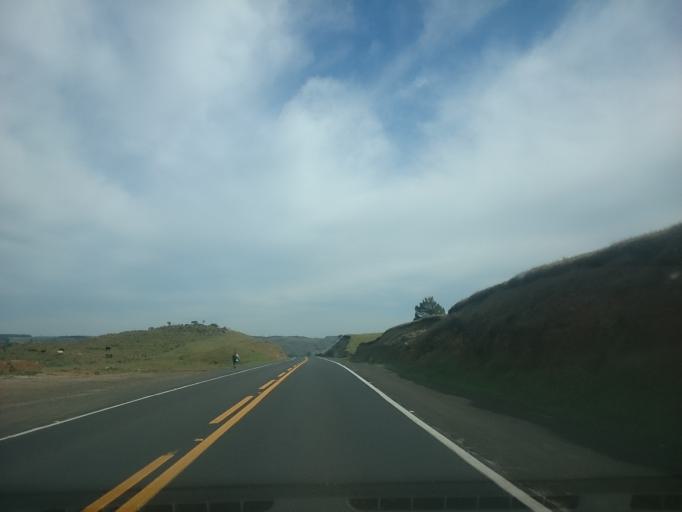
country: BR
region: Rio Grande do Sul
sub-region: Vacaria
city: Estrela
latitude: -28.0888
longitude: -50.5947
